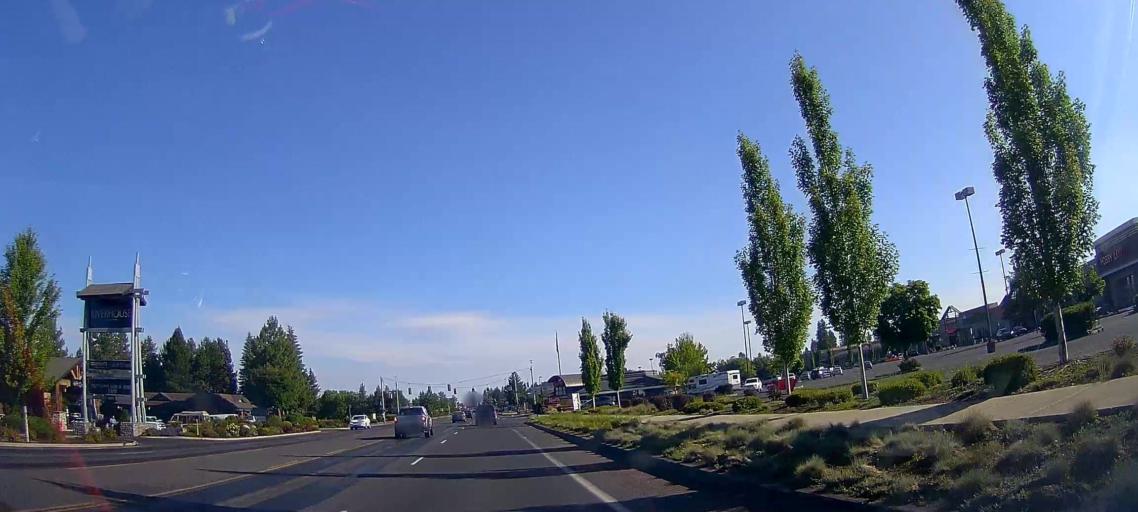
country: US
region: Oregon
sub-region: Deschutes County
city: Bend
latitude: 44.0805
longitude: -121.3050
